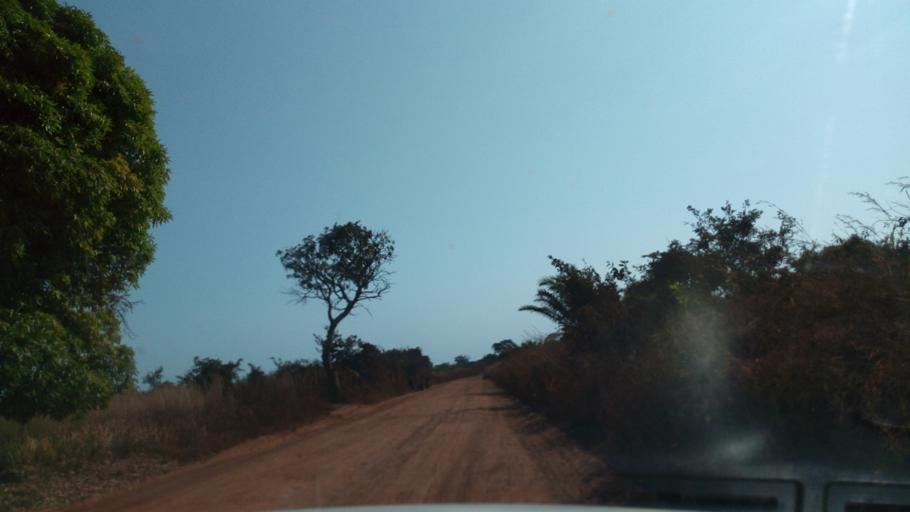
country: ZM
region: Luapula
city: Nchelenge
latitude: -9.1467
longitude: 28.2905
